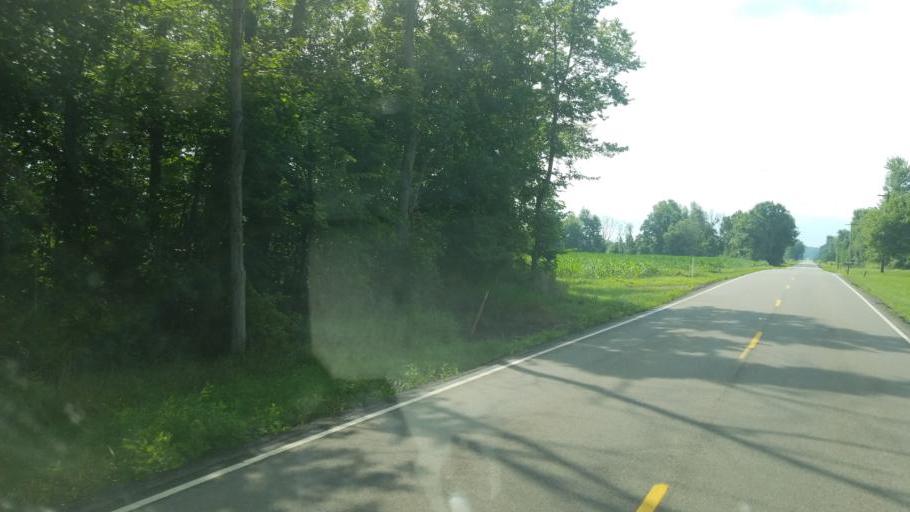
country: US
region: Ohio
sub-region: Licking County
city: Utica
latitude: 40.2320
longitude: -82.5664
